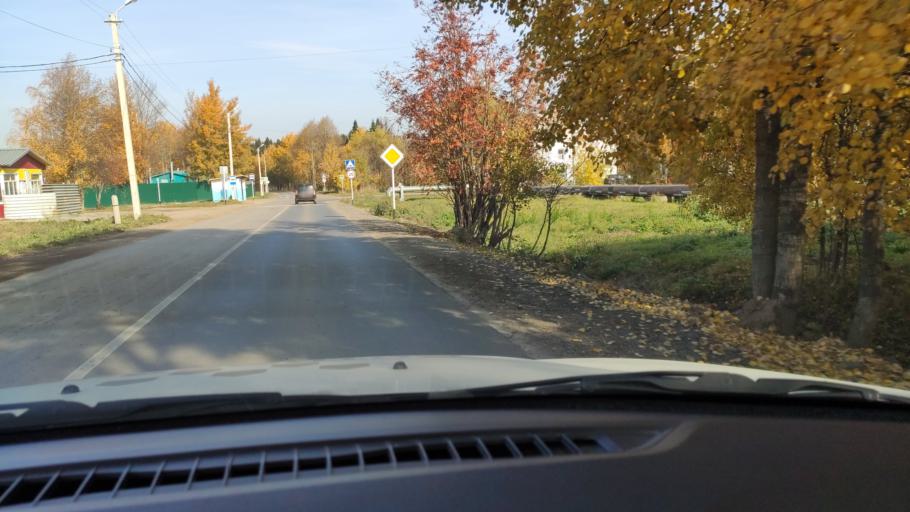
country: RU
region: Perm
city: Sylva
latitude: 58.0296
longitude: 56.7403
